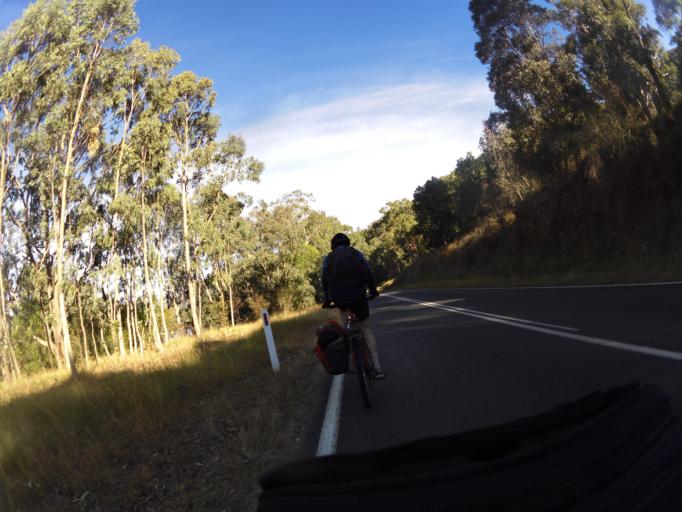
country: AU
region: New South Wales
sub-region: Greater Hume Shire
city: Holbrook
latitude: -35.9773
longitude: 147.8134
